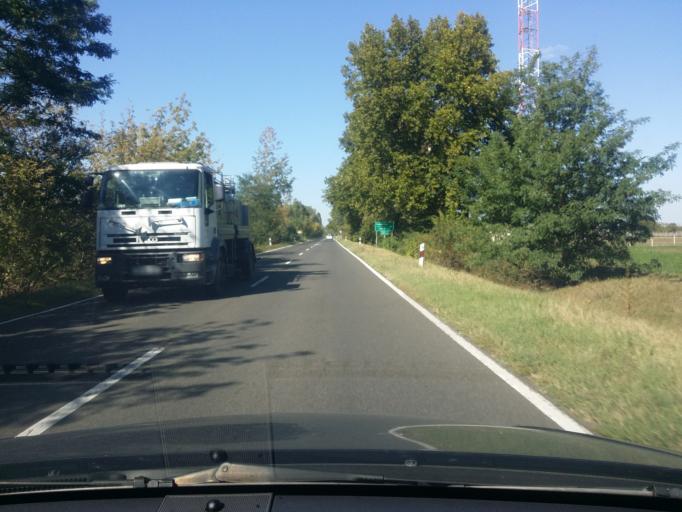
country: HU
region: Bacs-Kiskun
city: Palmonostora
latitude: 46.6073
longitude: 19.9166
